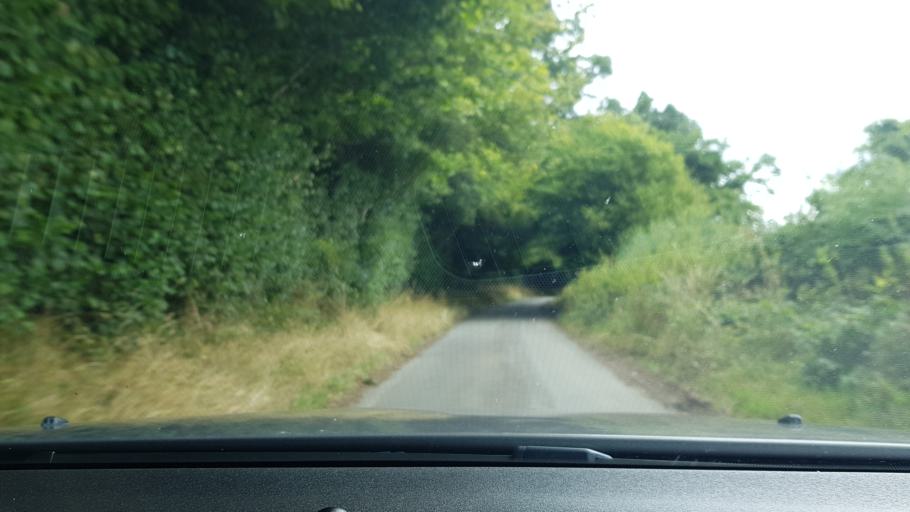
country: GB
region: England
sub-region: Wiltshire
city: Chilton Foliat
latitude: 51.4527
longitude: -1.5251
